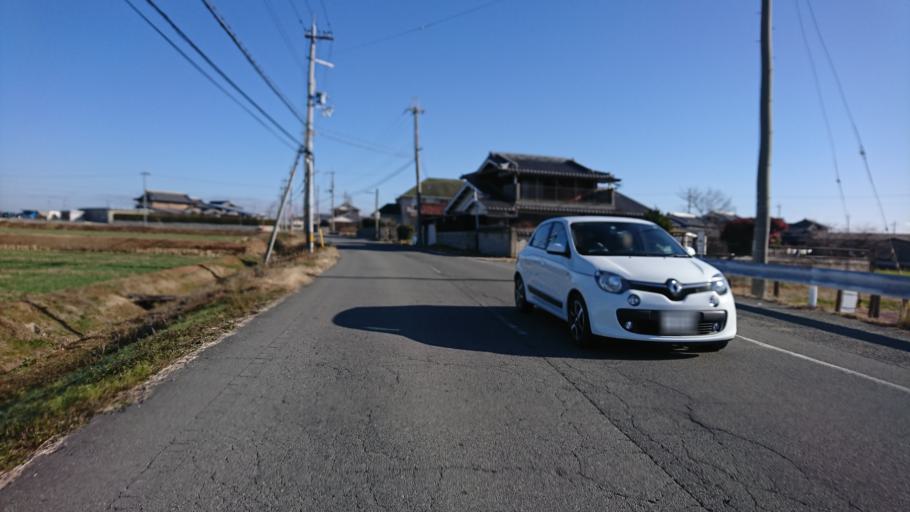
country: JP
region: Hyogo
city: Kakogawacho-honmachi
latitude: 34.7578
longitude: 134.8987
